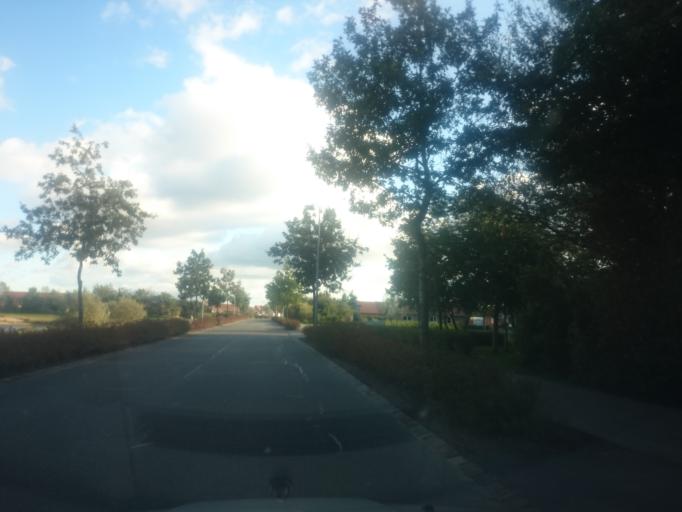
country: DK
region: South Denmark
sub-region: Billund Kommune
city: Billund
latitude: 55.7228
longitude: 9.1138
